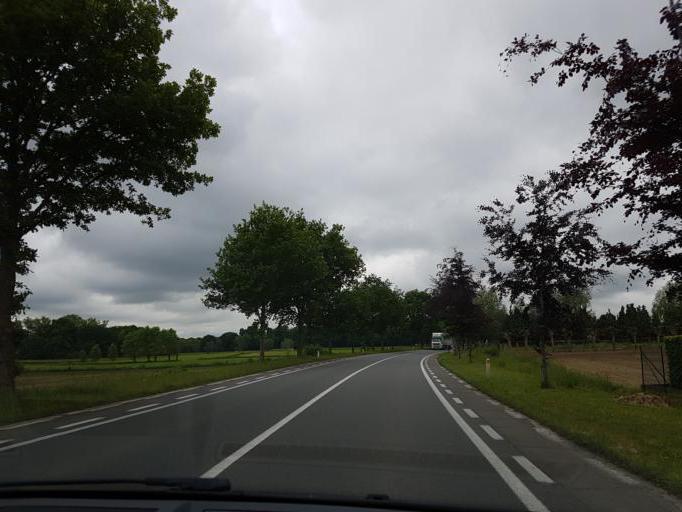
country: BE
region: Flanders
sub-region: Provincie West-Vlaanderen
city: Beernem
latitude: 51.1234
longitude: 3.3674
